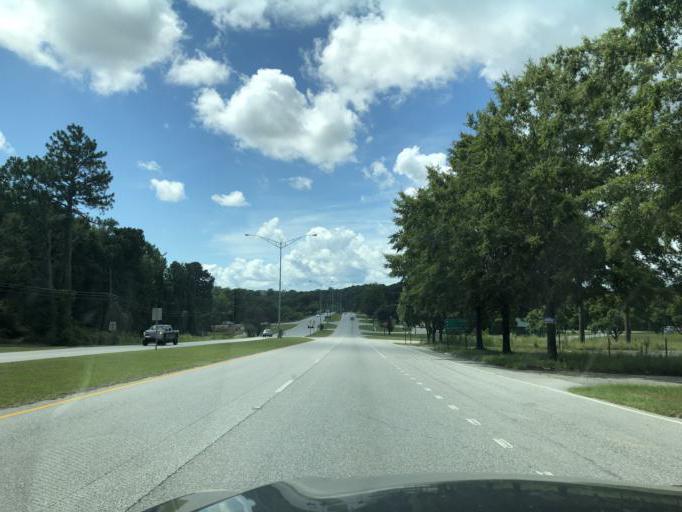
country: US
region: Alabama
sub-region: Barbour County
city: Eufaula
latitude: 31.9129
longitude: -85.1486
